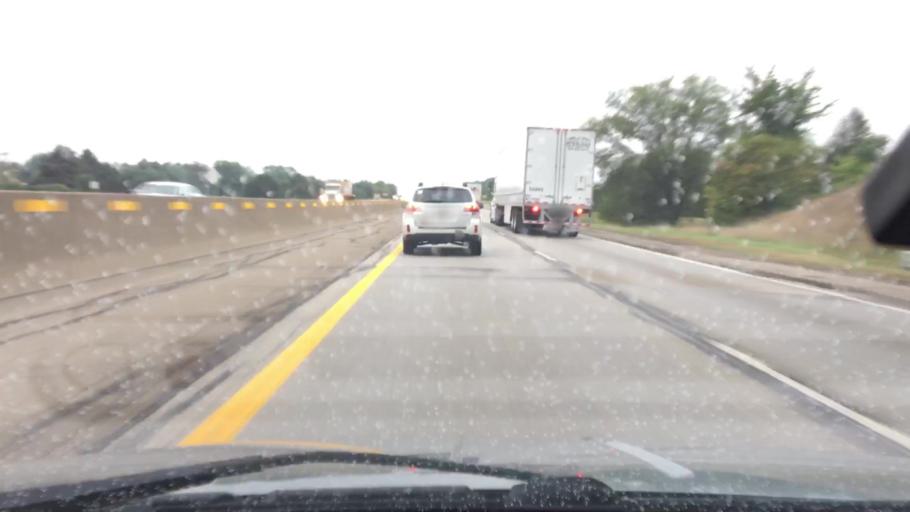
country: US
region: Michigan
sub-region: Kalamazoo County
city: Portage
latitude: 42.2464
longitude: -85.5564
